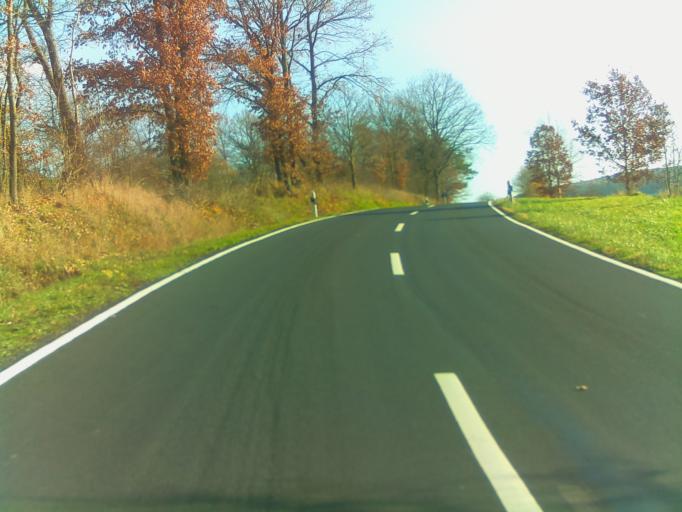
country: DE
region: Bavaria
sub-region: Regierungsbezirk Unterfranken
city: Bad Bocklet
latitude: 50.2988
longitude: 10.1154
